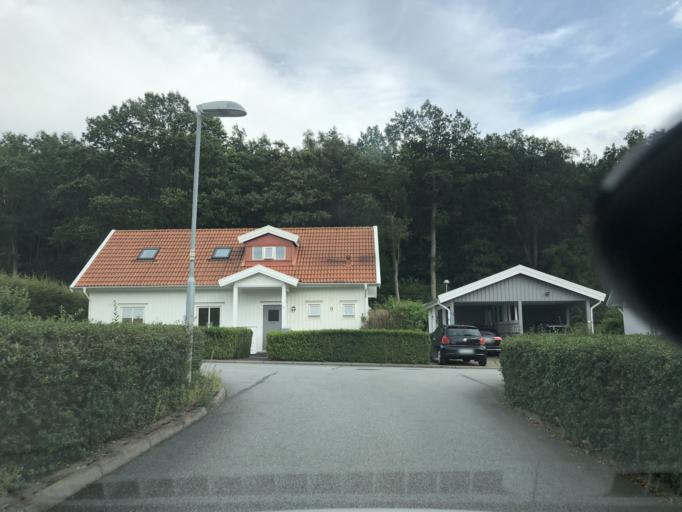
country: SE
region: Vaestra Goetaland
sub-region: Goteborg
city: Goeteborg
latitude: 57.7515
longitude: 11.9626
